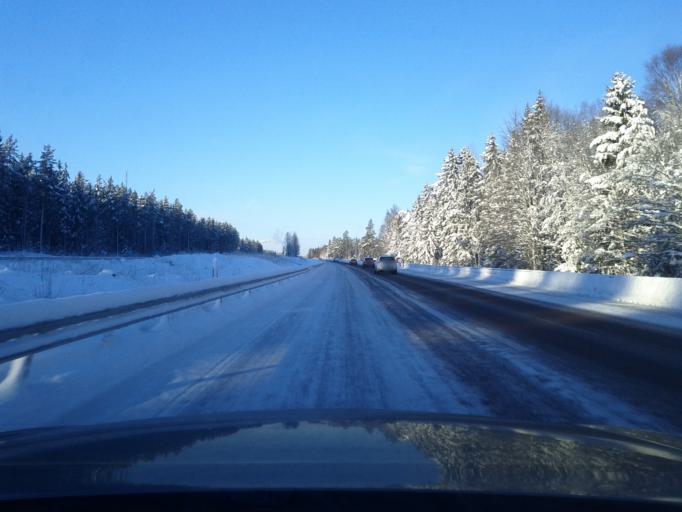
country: SE
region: Gaevleborg
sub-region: Gavle Kommun
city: Gavle
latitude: 60.6082
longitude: 17.1770
